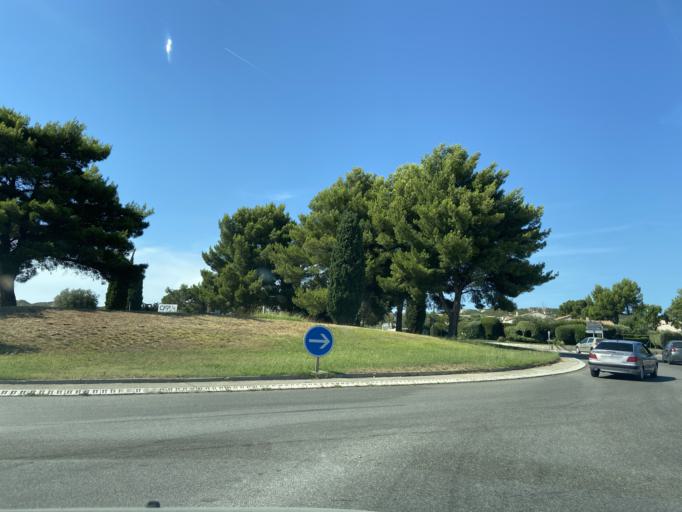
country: FR
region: Provence-Alpes-Cote d'Azur
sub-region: Departement des Bouches-du-Rhone
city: La Fare-les-Oliviers
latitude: 43.5495
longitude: 5.1822
